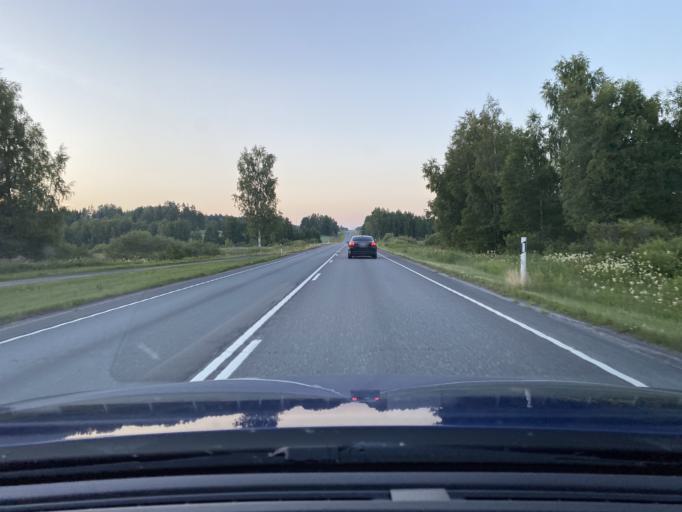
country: FI
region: Pirkanmaa
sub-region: Luoteis-Pirkanmaa
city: Ikaalinen
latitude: 61.8668
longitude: 22.9623
